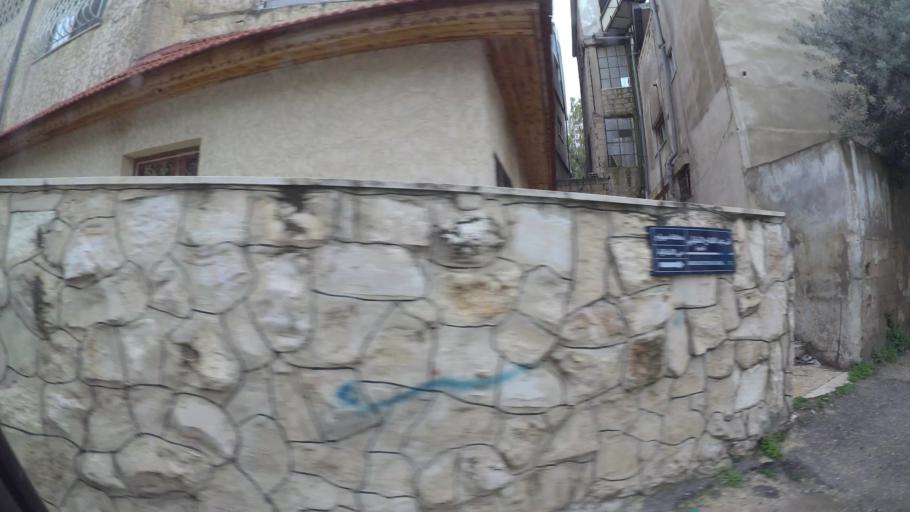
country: JO
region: Amman
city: Al Jubayhah
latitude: 32.0286
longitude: 35.8337
